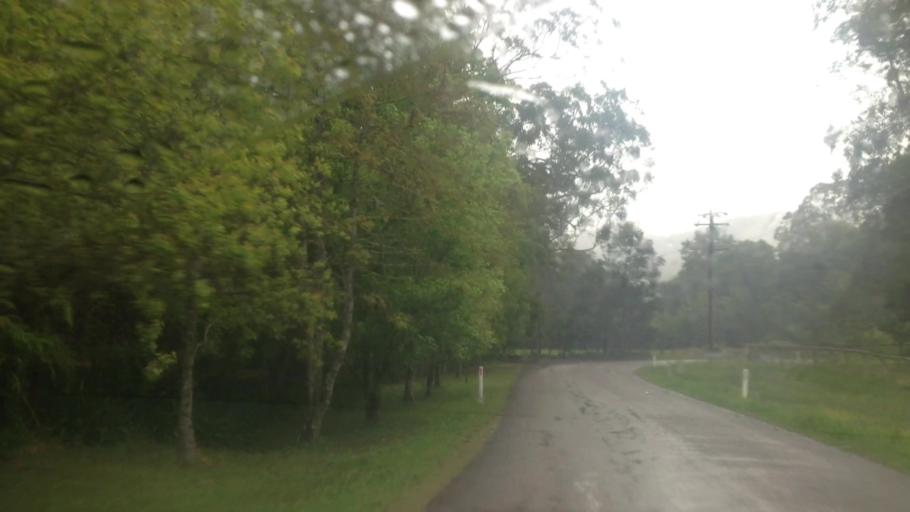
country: AU
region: New South Wales
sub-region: Wyong Shire
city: Little Jilliby
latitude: -33.1898
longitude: 151.3607
